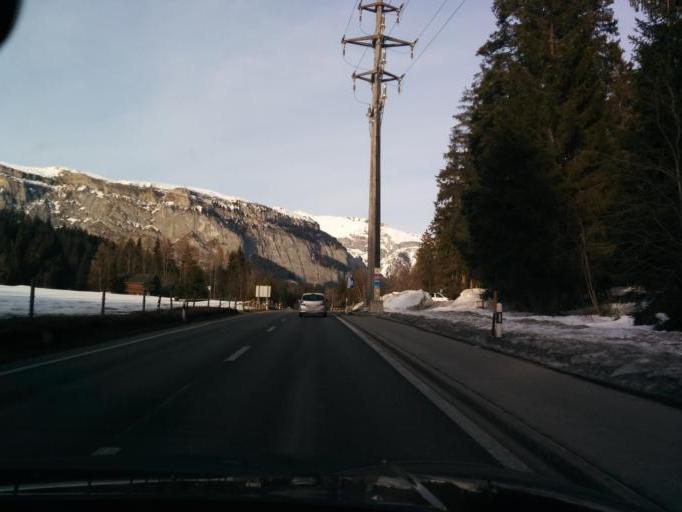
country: CH
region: Grisons
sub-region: Surselva District
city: Laax
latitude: 46.8209
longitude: 9.2692
